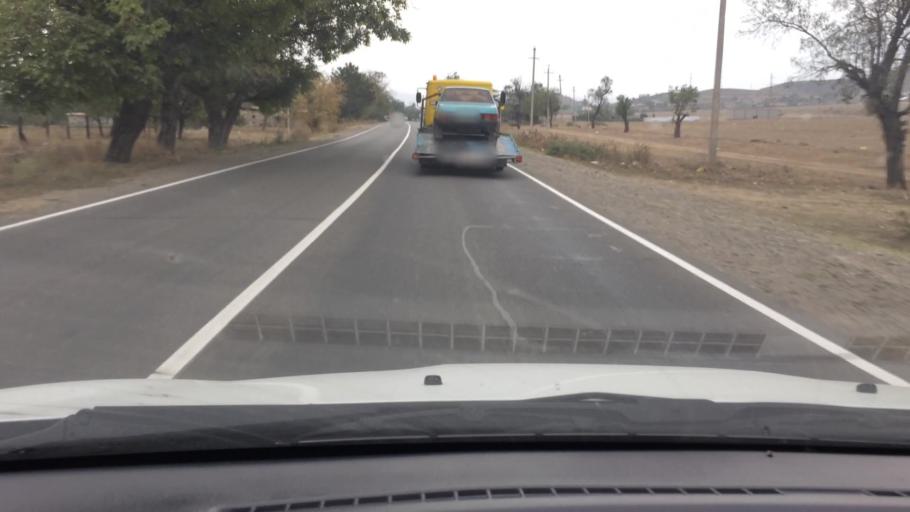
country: GE
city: Naghvarevi
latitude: 41.3799
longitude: 44.8321
